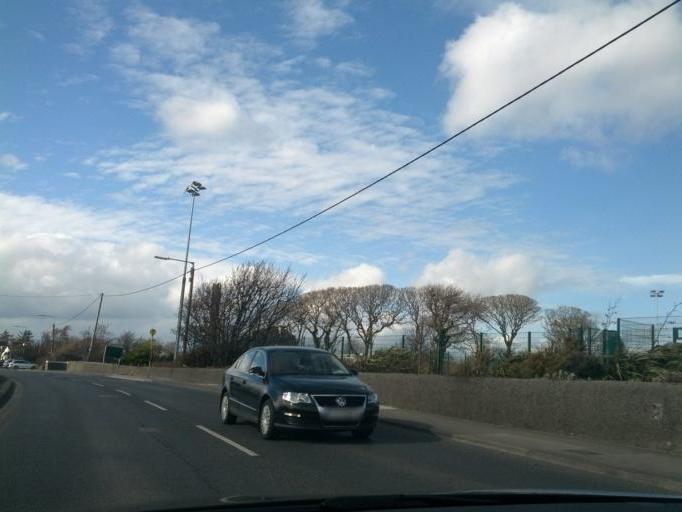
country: IE
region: Leinster
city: Sutton
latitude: 53.3861
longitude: -6.1024
